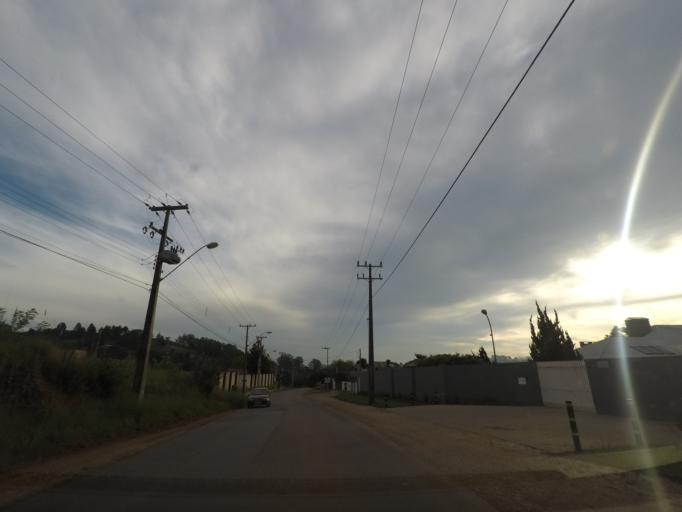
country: BR
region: Parana
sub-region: Colombo
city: Colombo
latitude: -25.2866
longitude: -49.2125
